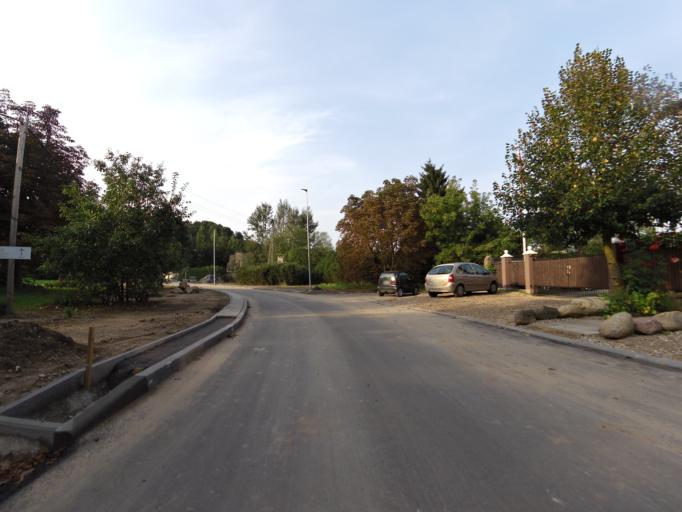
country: LT
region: Vilnius County
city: Lazdynai
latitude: 54.6809
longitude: 25.2268
